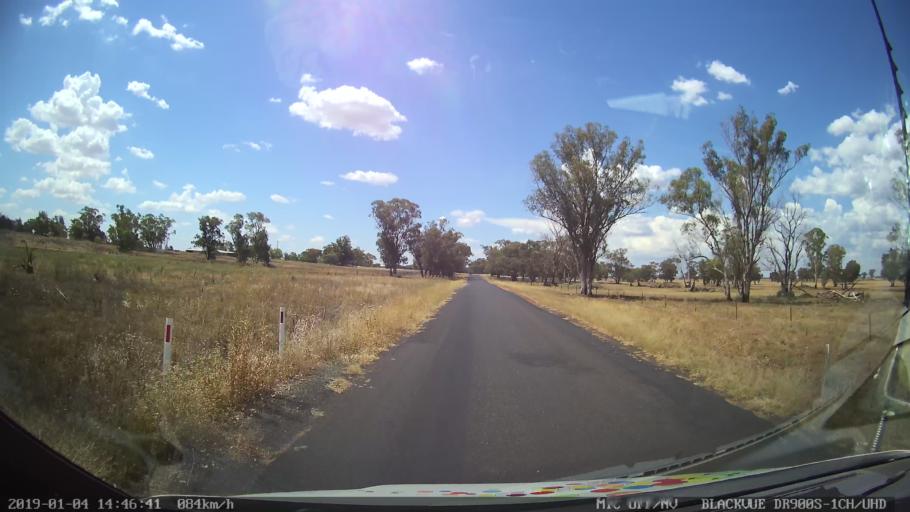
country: AU
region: New South Wales
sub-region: Dubbo Municipality
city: Dubbo
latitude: -32.0784
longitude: 148.6587
